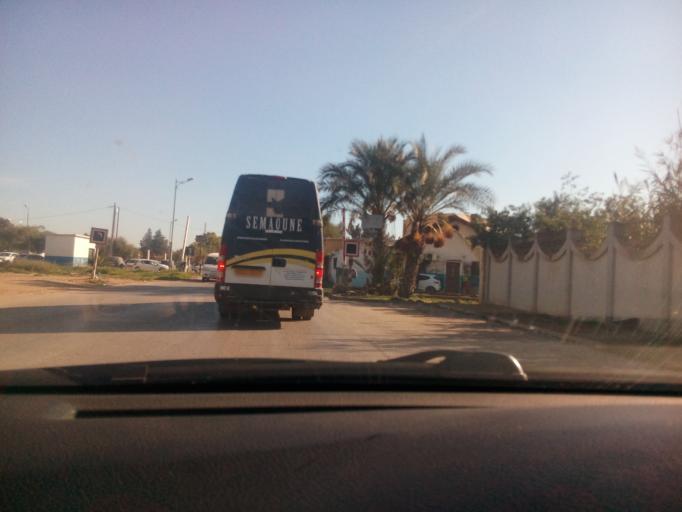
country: DZ
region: Oran
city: Es Senia
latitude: 35.6379
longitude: -0.6116
